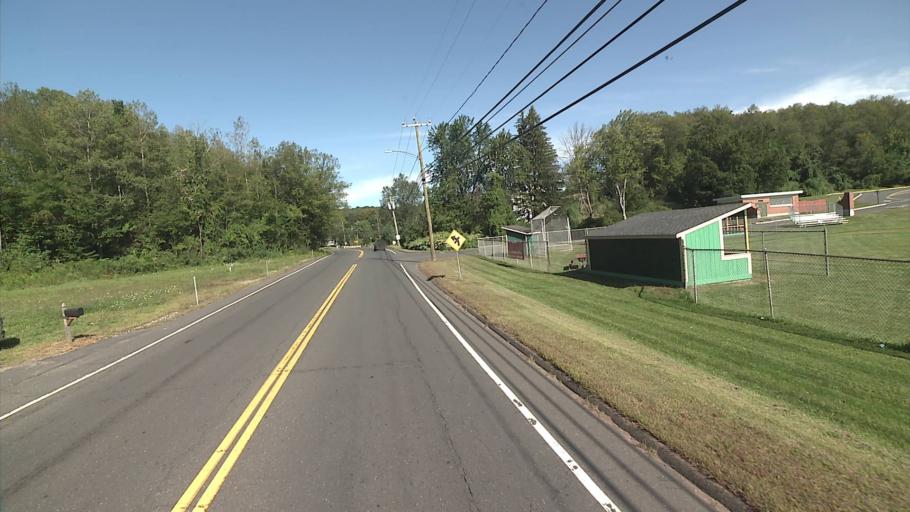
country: US
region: Connecticut
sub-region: New Haven County
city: Prospect
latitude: 41.5367
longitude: -72.9401
